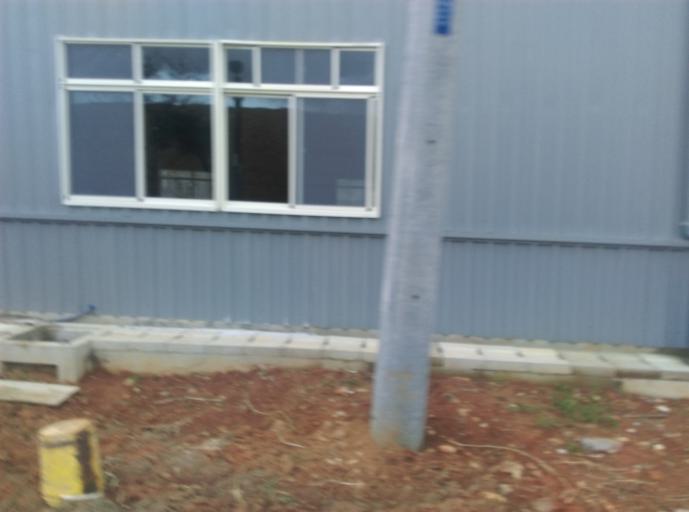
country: TW
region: Taiwan
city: Taoyuan City
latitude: 24.9971
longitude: 121.2507
